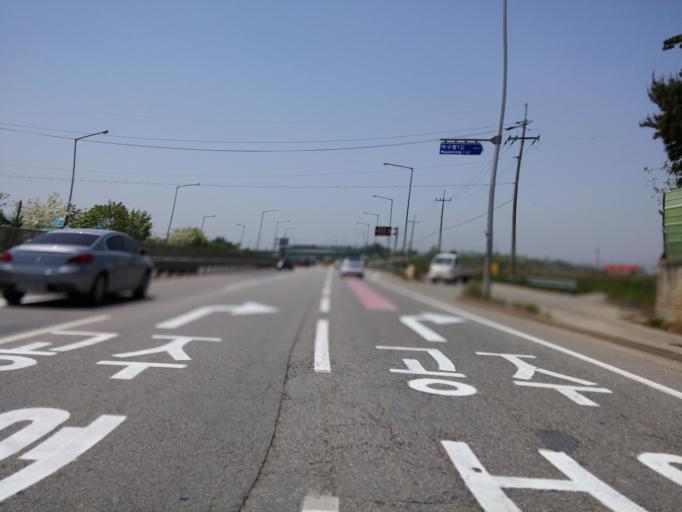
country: KR
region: Chungcheongnam-do
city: Nonsan
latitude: 36.2136
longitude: 127.1244
